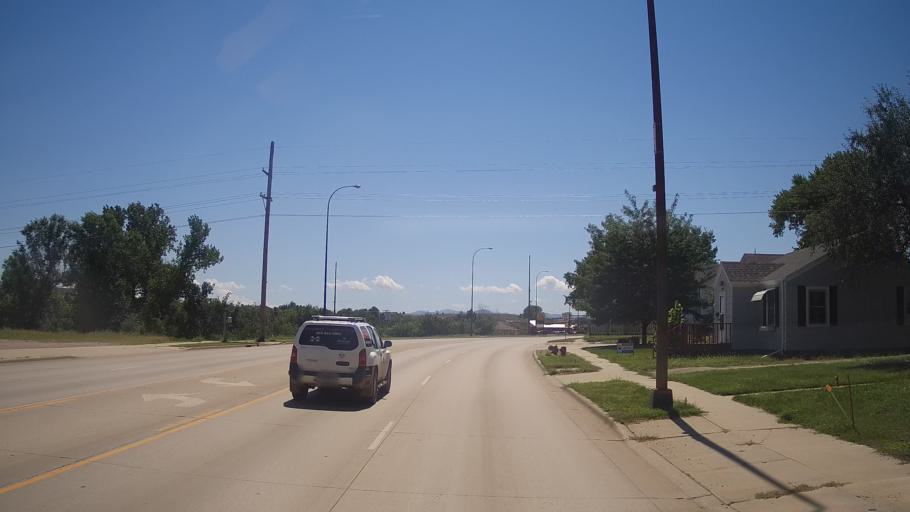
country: US
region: South Dakota
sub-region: Butte County
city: Belle Fourche
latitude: 44.6652
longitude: -103.8538
